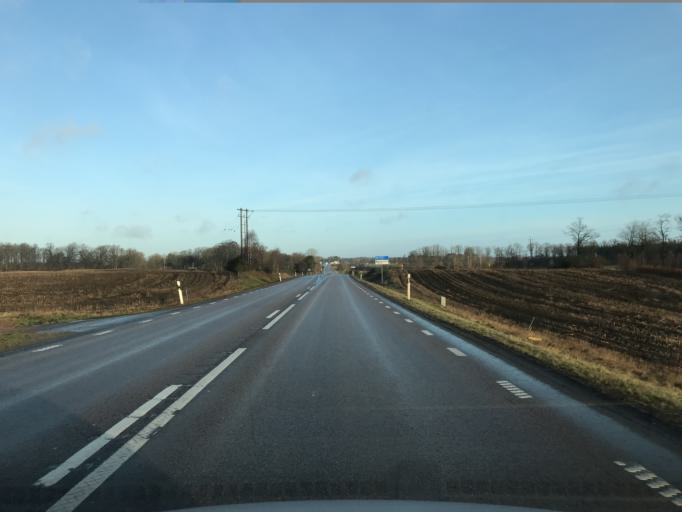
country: SE
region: Skane
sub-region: Hassleholms Kommun
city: Hassleholm
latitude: 56.1852
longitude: 13.7535
